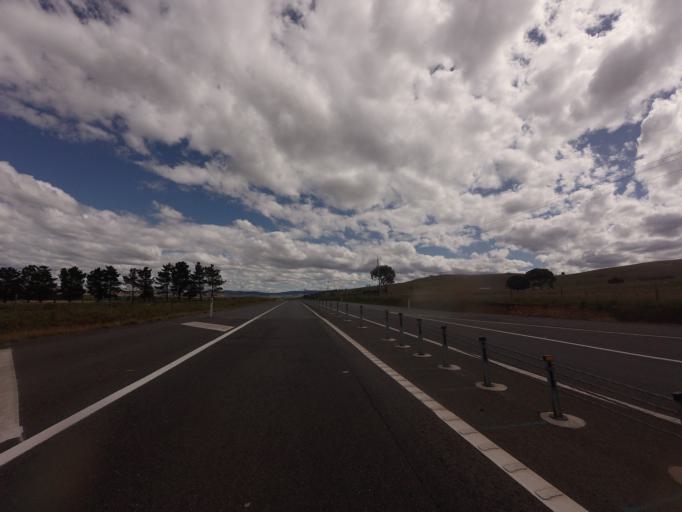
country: AU
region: Tasmania
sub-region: Northern Midlands
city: Evandale
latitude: -42.1128
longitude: 147.4434
